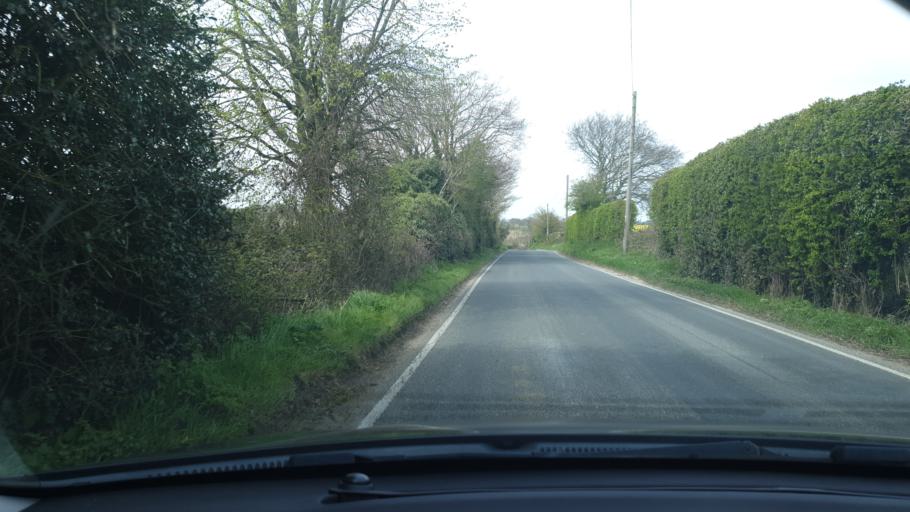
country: GB
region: England
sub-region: Essex
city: Little Clacton
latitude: 51.9023
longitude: 1.1817
